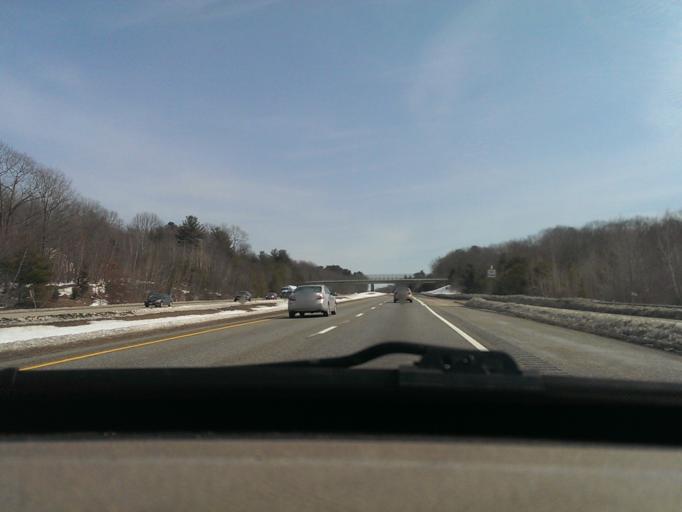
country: US
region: Massachusetts
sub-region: Worcester County
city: Millville
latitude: 42.0209
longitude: -71.5997
